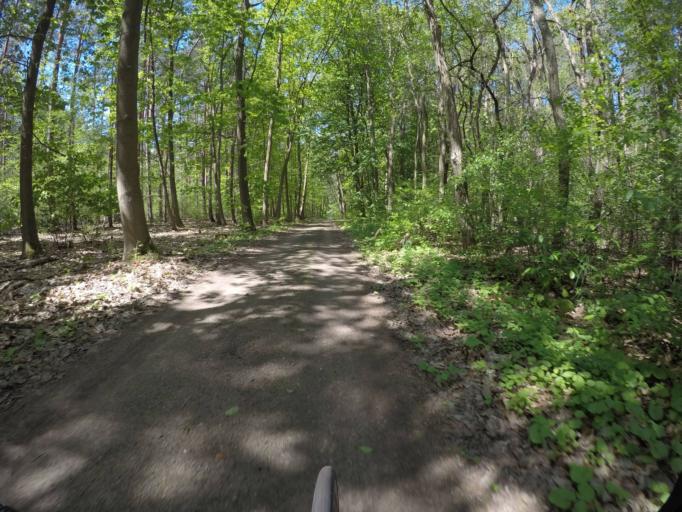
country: DE
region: Brandenburg
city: Potsdam
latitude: 52.4547
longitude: 13.0785
